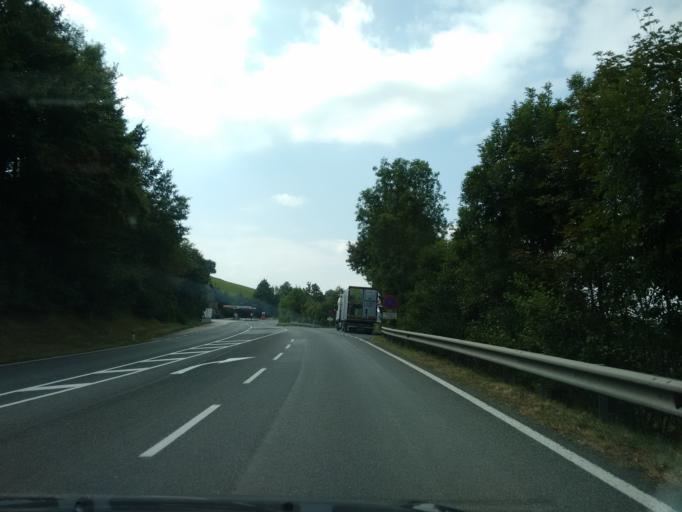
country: AT
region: Upper Austria
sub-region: Politischer Bezirk Grieskirchen
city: Bad Schallerbach
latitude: 48.2234
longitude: 13.9175
